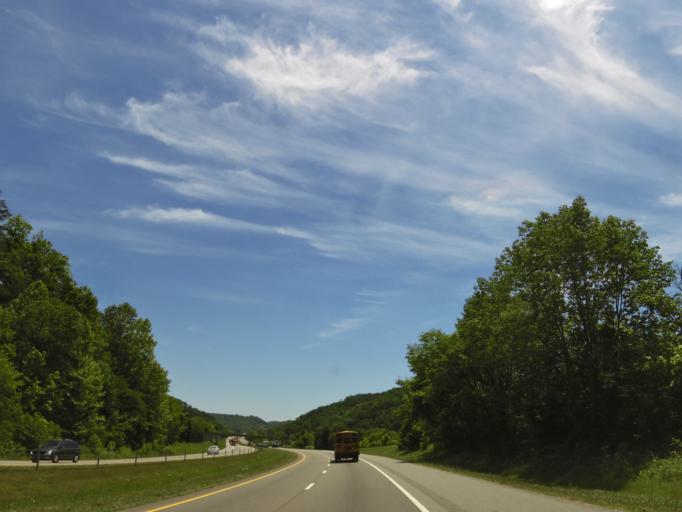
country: US
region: Tennessee
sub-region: Anderson County
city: Norris
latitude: 36.1516
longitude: -84.0660
